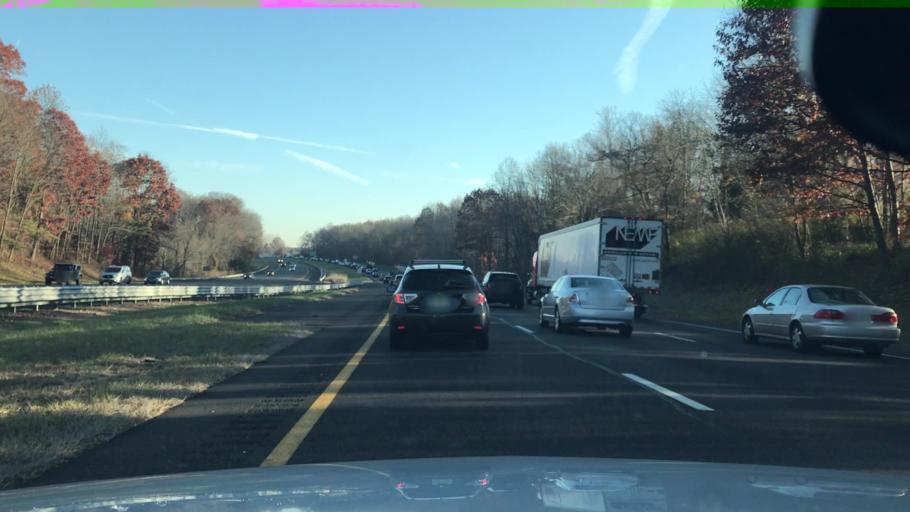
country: US
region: New Jersey
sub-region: Burlington County
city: Bordentown
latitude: 40.1149
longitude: -74.7264
